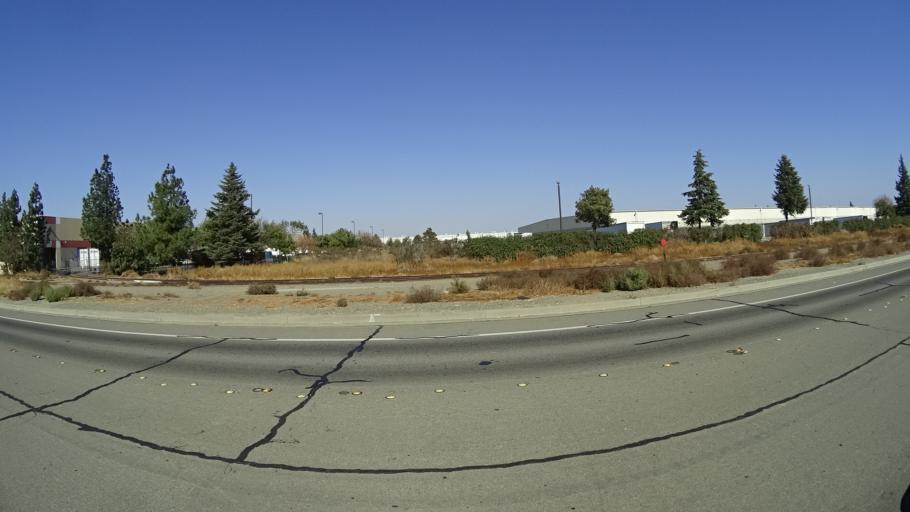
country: US
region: California
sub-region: Yolo County
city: Woodland
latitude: 38.6770
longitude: -121.7217
